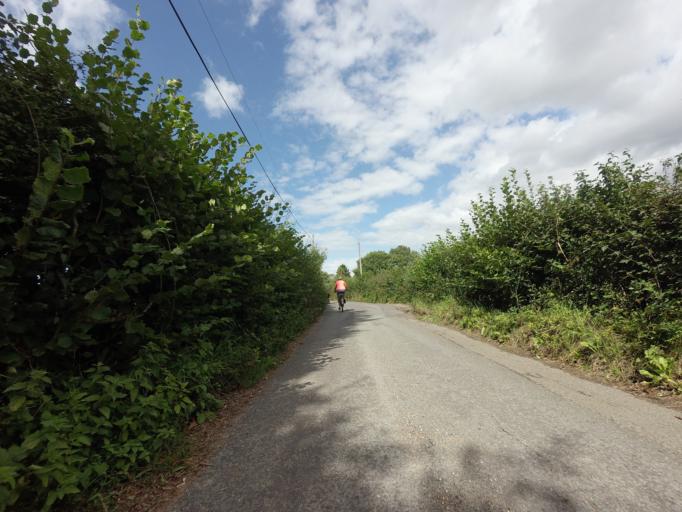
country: GB
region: England
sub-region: Kent
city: Shoreham
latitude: 51.3073
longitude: 0.1799
